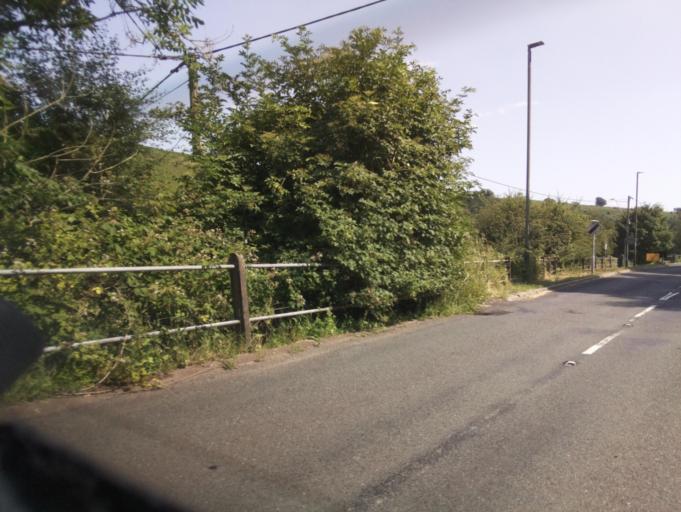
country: GB
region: Wales
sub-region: Caerphilly County Borough
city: New Tredegar
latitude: 51.7085
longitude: -3.2287
